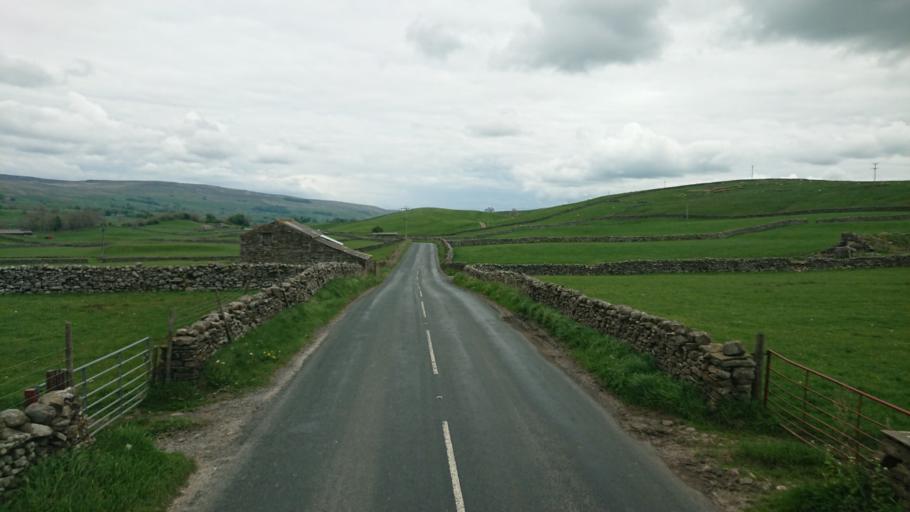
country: GB
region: England
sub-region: County Durham
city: Bowes
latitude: 54.3035
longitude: -2.1366
